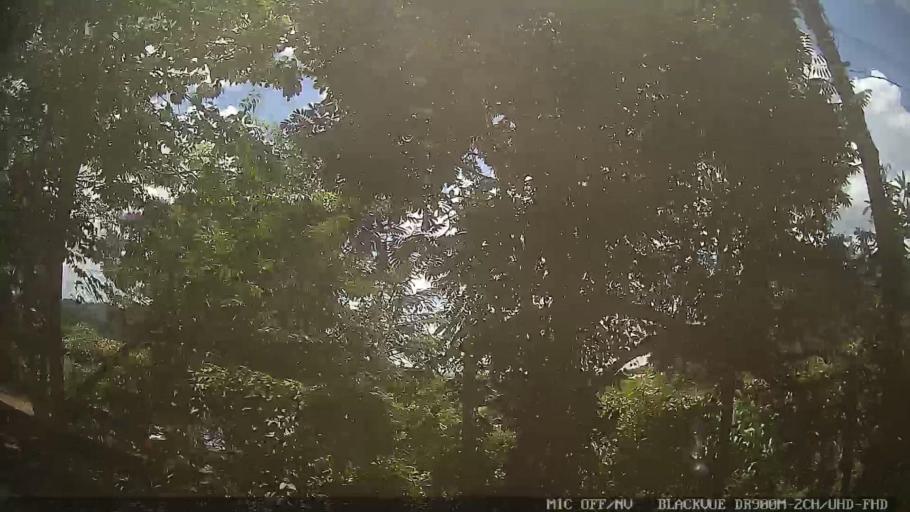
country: BR
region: Sao Paulo
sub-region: Braganca Paulista
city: Braganca Paulista
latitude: -23.0319
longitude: -46.5251
